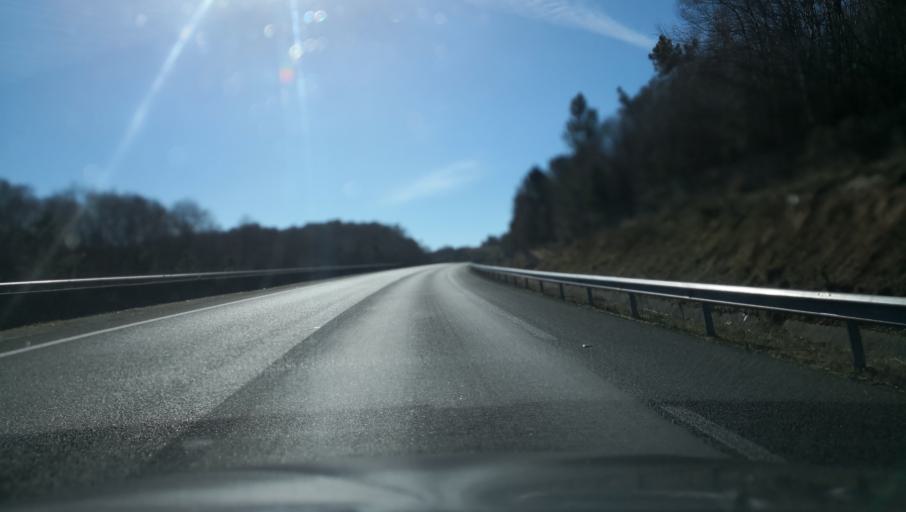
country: ES
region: Galicia
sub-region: Provincia de Pontevedra
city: Lalin
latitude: 42.6571
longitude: -8.1406
